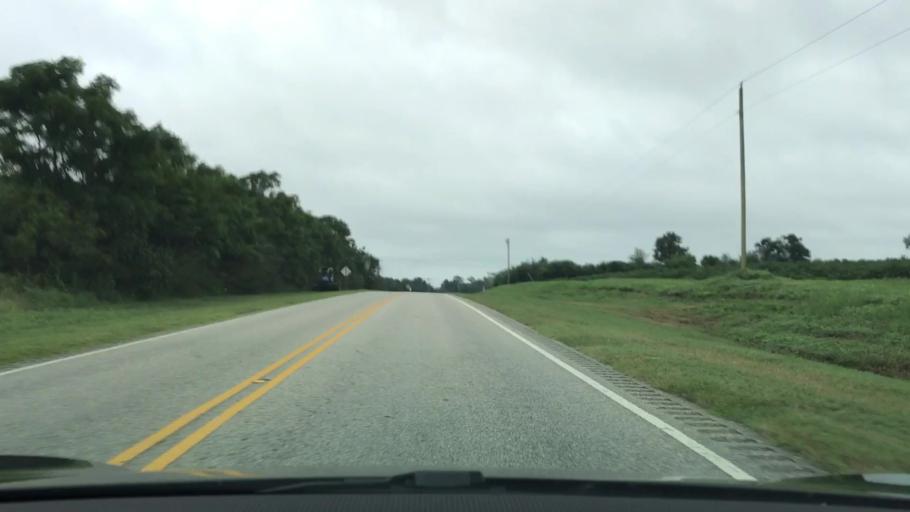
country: US
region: Alabama
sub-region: Coffee County
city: Elba
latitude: 31.3366
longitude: -86.1314
